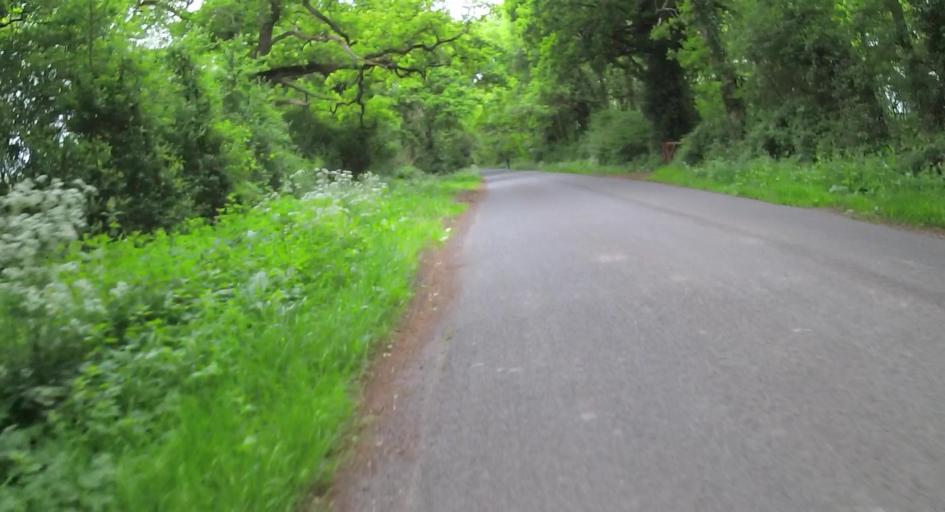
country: GB
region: England
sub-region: West Berkshire
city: Stratfield Mortimer
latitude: 51.3668
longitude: -1.0342
